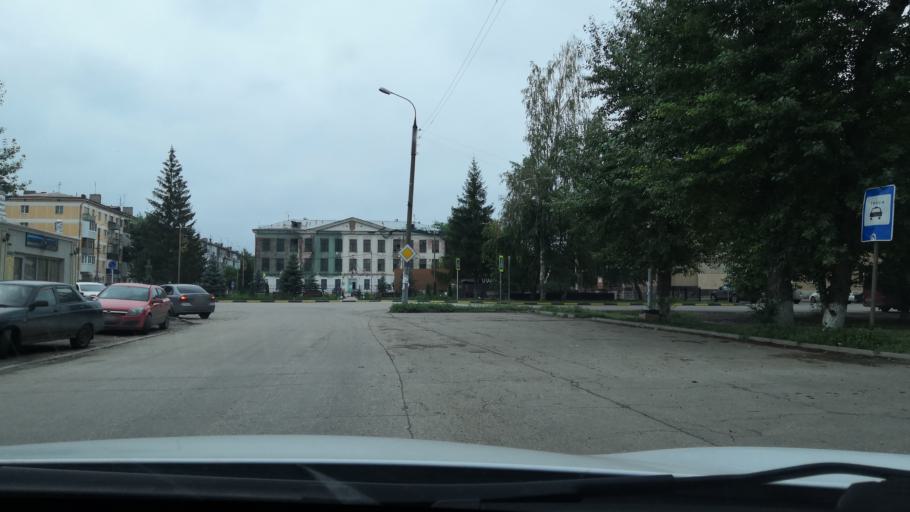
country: RU
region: Samara
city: Smyshlyayevka
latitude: 53.2698
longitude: 50.3943
